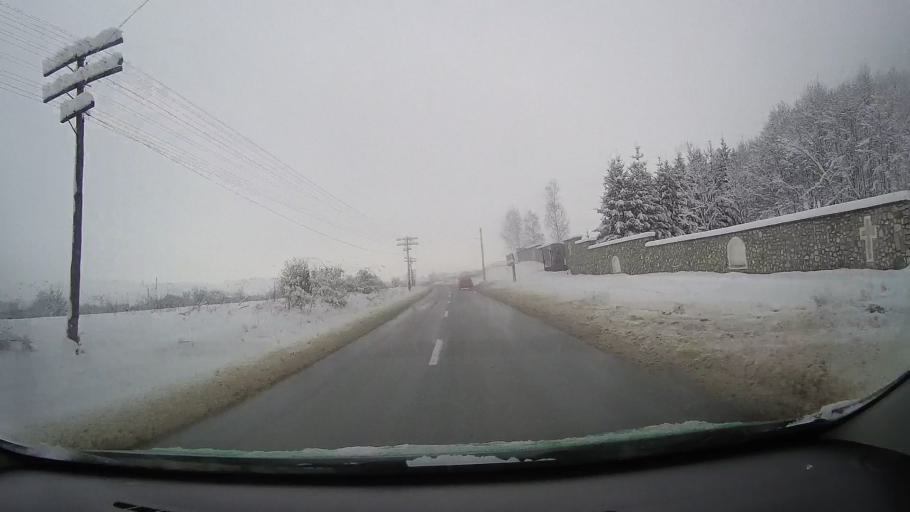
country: RO
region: Sibiu
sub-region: Comuna Orlat
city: Orlat
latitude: 45.7573
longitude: 23.9460
